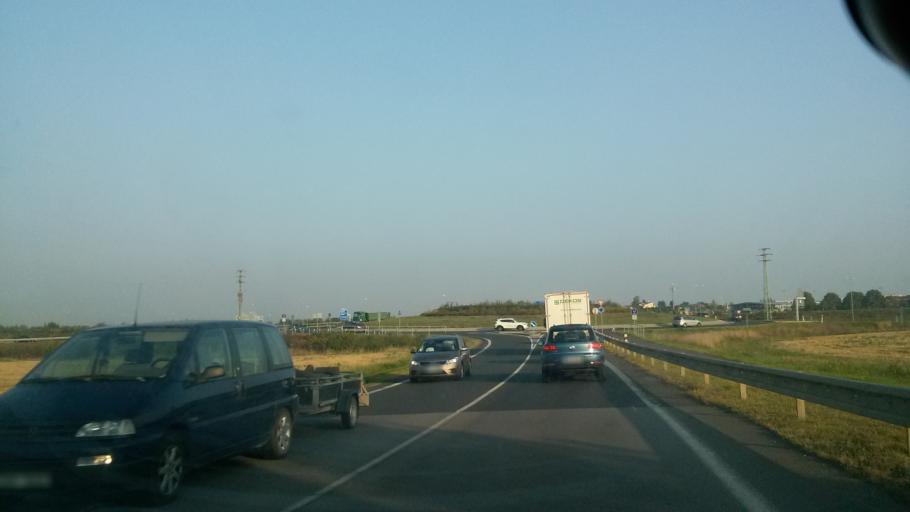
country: CZ
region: Central Bohemia
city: Jesenice
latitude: 49.9602
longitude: 14.5268
